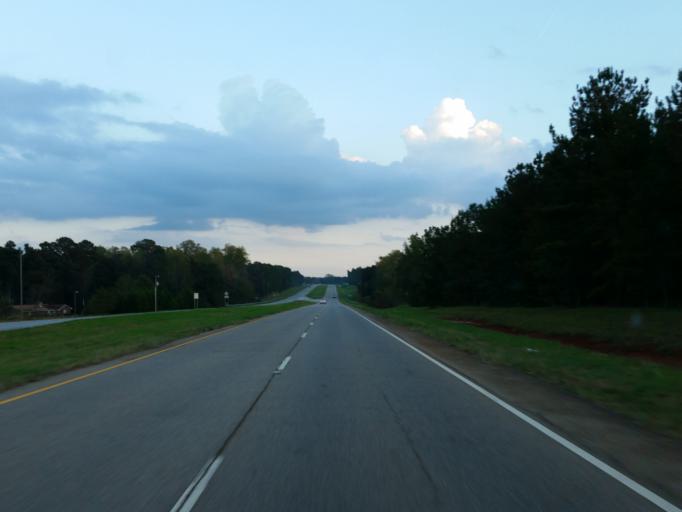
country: US
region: Georgia
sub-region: Pulaski County
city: Hawkinsville
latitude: 32.3467
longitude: -83.5747
